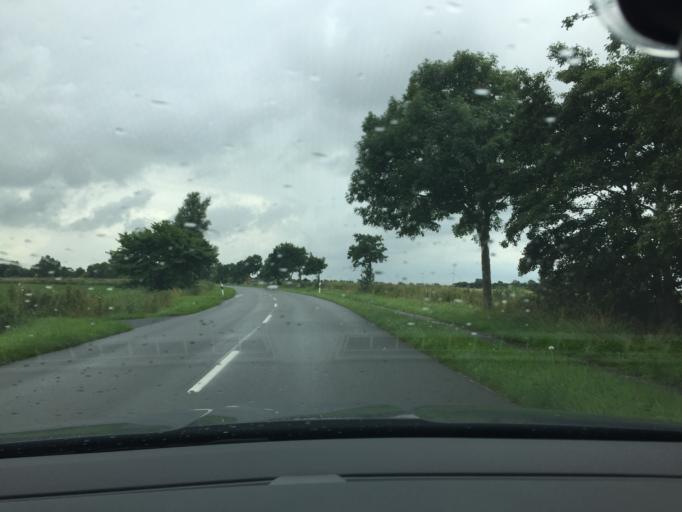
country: DE
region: Lower Saxony
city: Wirdum
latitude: 53.4937
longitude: 7.0668
